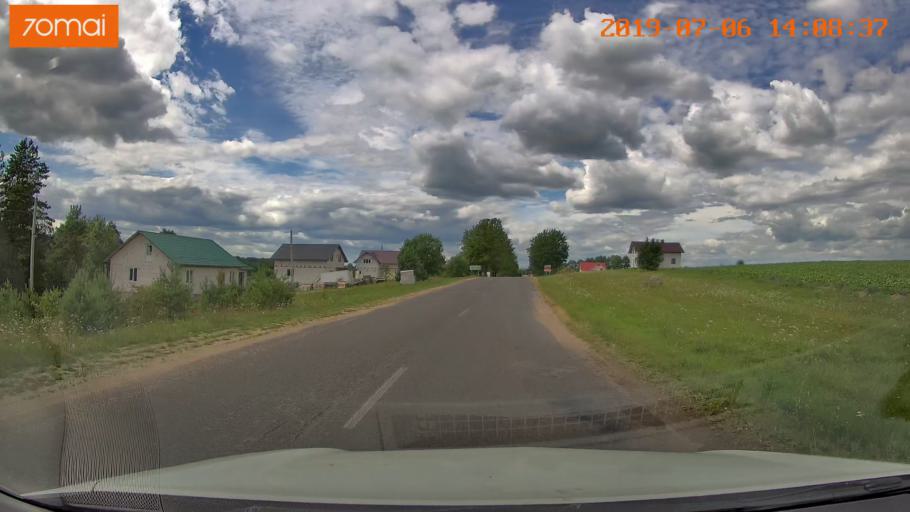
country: BY
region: Minsk
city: Ivyanyets
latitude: 53.8764
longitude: 26.7558
